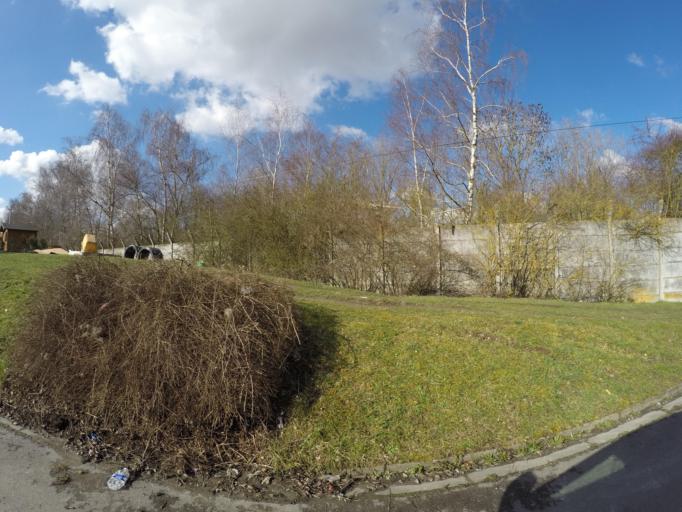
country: FR
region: Nord-Pas-de-Calais
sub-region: Departement du Pas-de-Calais
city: Bully-les-Mines
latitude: 50.4534
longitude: 2.7263
